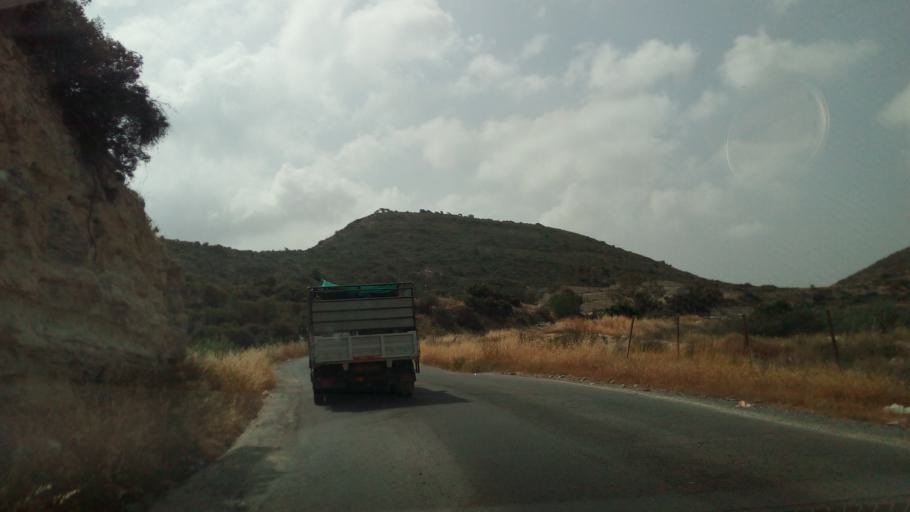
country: CY
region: Limassol
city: Pano Polemidia
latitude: 34.7489
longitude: 32.9540
